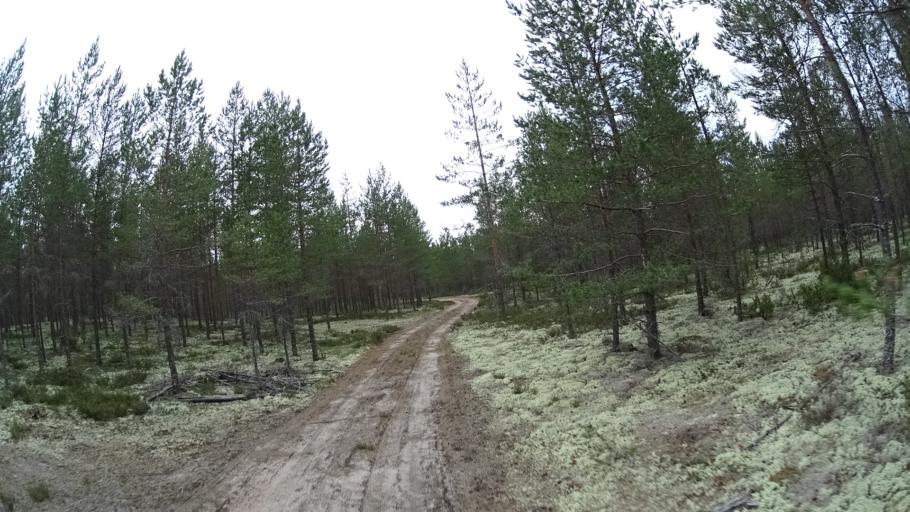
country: FI
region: Satakunta
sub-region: Pohjois-Satakunta
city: Jaemijaervi
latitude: 61.7615
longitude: 22.7868
